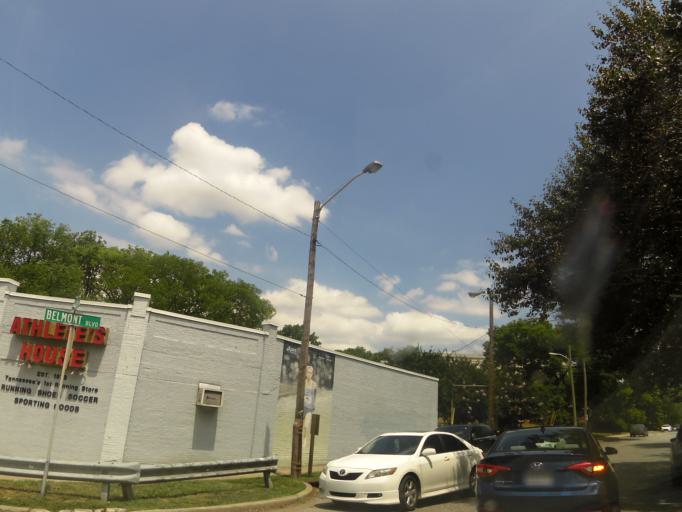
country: US
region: Tennessee
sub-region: Davidson County
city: Nashville
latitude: 36.1329
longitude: -86.7959
